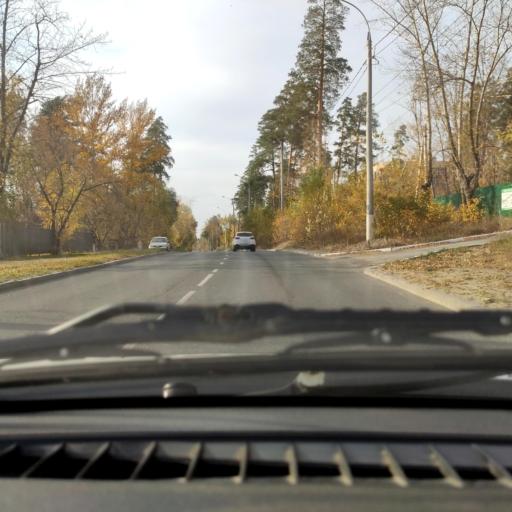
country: RU
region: Samara
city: Tol'yatti
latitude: 53.4749
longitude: 49.3767
